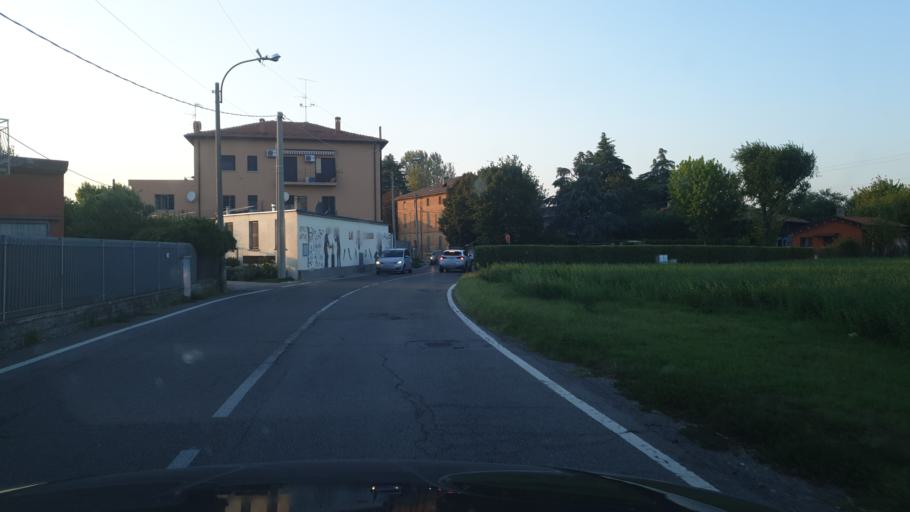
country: IT
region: Emilia-Romagna
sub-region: Provincia di Bologna
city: Quarto Inferiore
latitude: 44.5225
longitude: 11.3811
